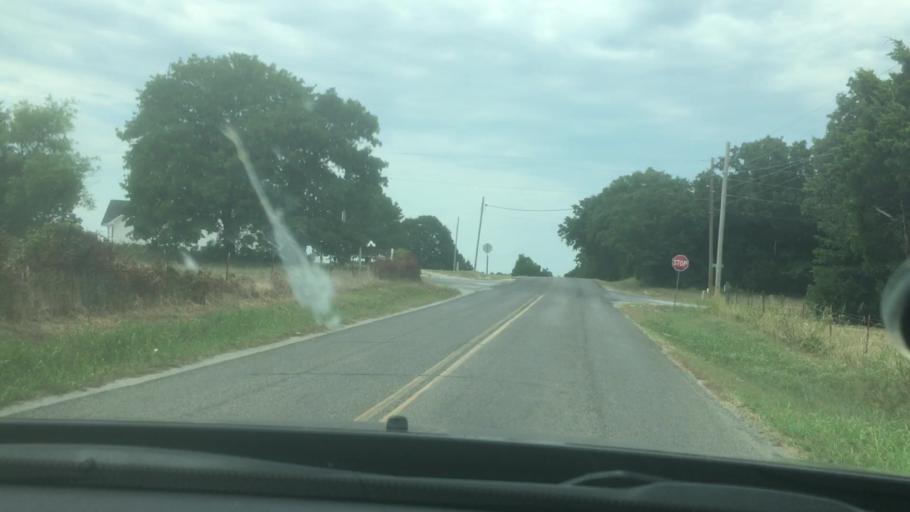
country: US
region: Oklahoma
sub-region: Murray County
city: Davis
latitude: 34.4911
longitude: -97.0555
